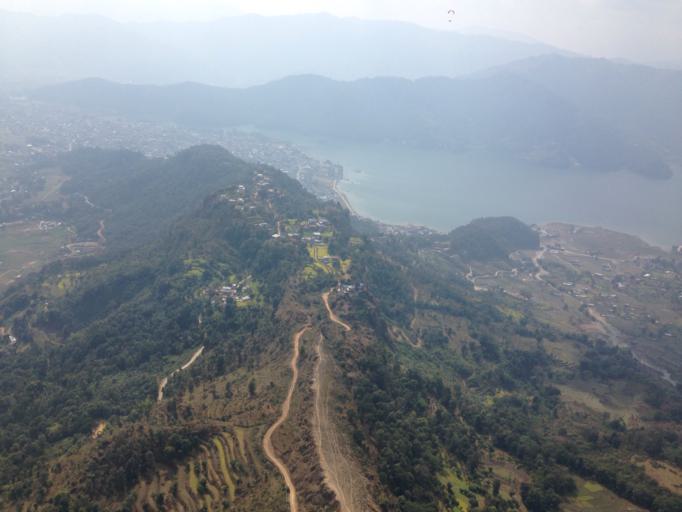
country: NP
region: Western Region
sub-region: Gandaki Zone
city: Pokhara
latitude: 28.2368
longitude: 83.9677
